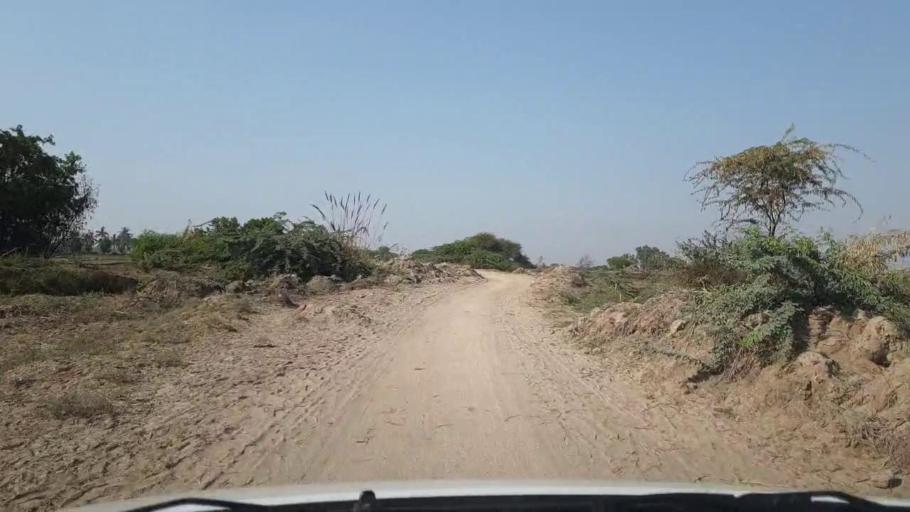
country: PK
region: Sindh
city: Mirpur Sakro
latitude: 24.5931
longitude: 67.6307
